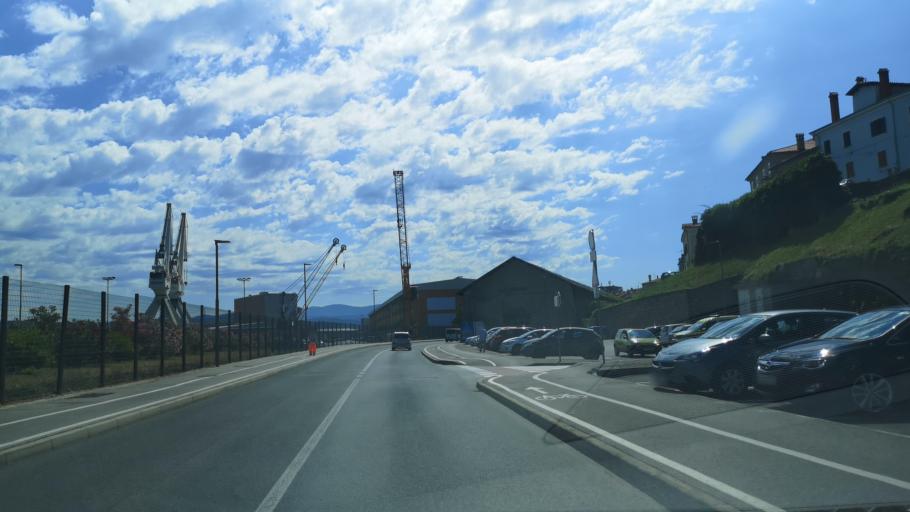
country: SI
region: Koper-Capodistria
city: Koper
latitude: 45.5500
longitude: 13.7305
